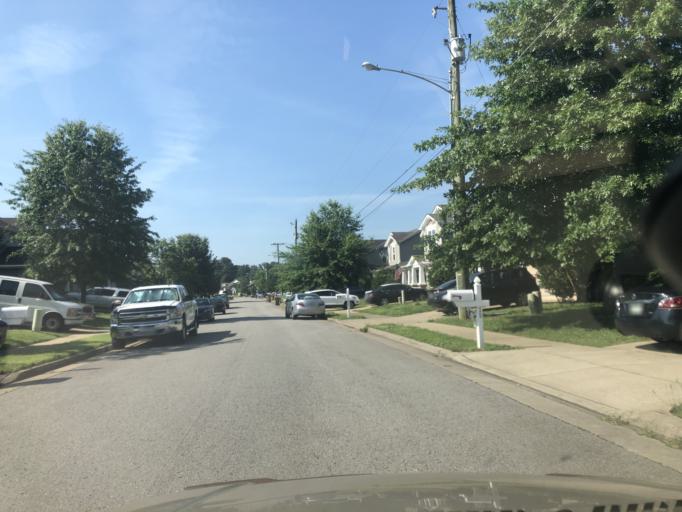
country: US
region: Tennessee
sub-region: Davidson County
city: Lakewood
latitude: 36.2376
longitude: -86.6944
